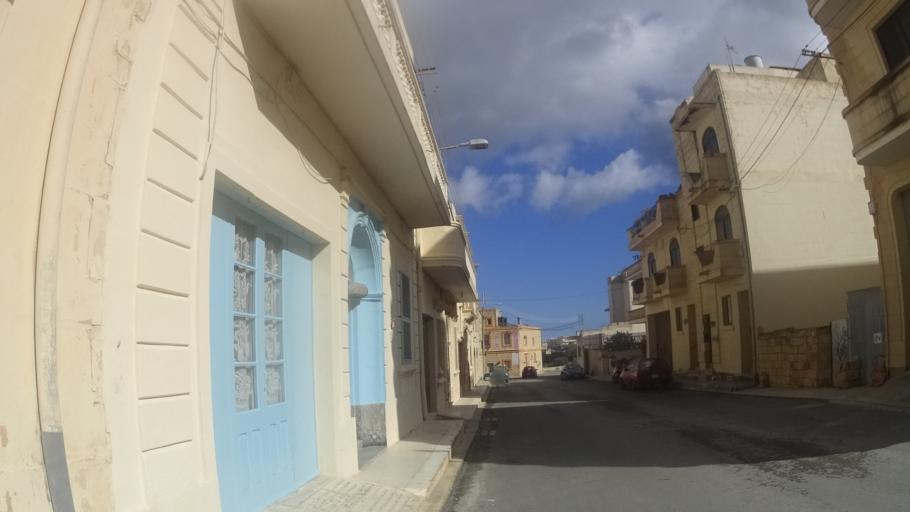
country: MT
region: In-Nadur
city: Nadur
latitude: 36.0421
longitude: 14.2891
